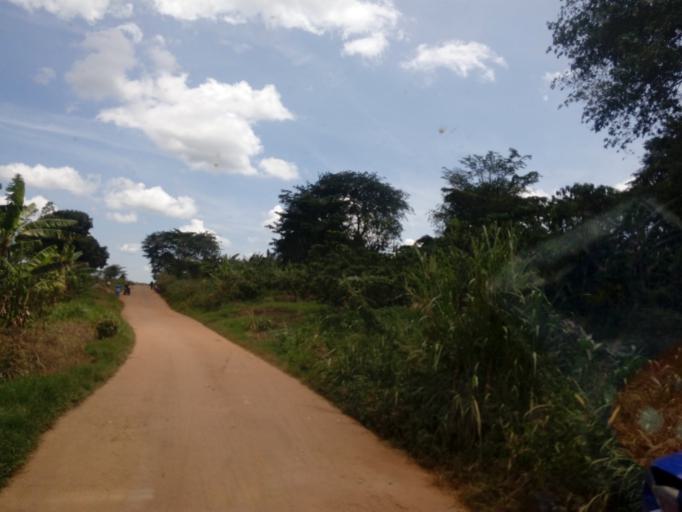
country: UG
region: Central Region
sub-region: Mubende District
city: Mubende
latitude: 0.4543
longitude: 31.6934
